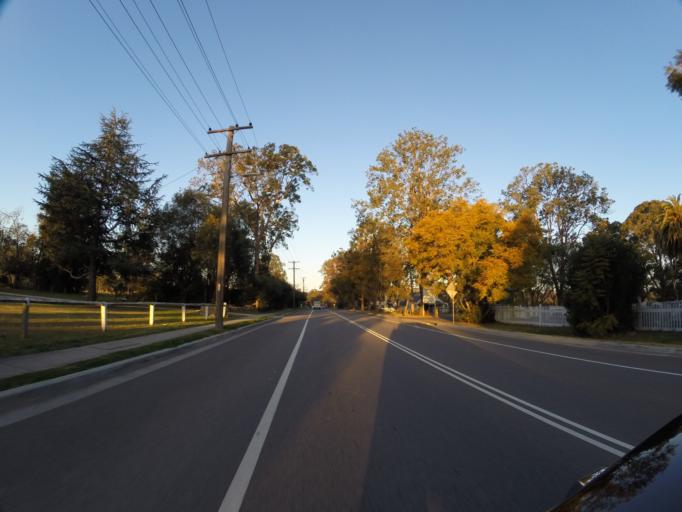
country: AU
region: New South Wales
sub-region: Camden
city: Cobbitty
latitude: -34.0156
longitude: 150.6883
